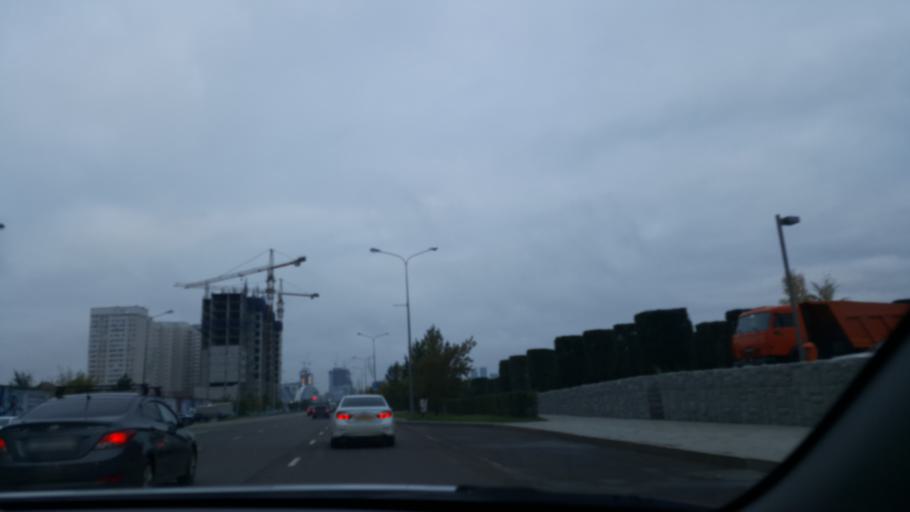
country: KZ
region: Astana Qalasy
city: Astana
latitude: 51.1204
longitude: 71.4636
